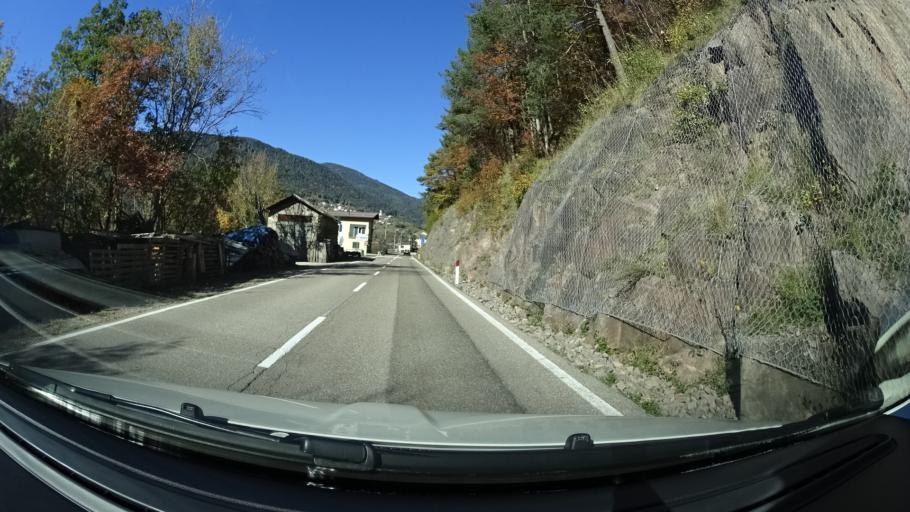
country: IT
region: Trentino-Alto Adige
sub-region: Provincia di Trento
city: Valfloriana
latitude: 46.2469
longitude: 11.3432
